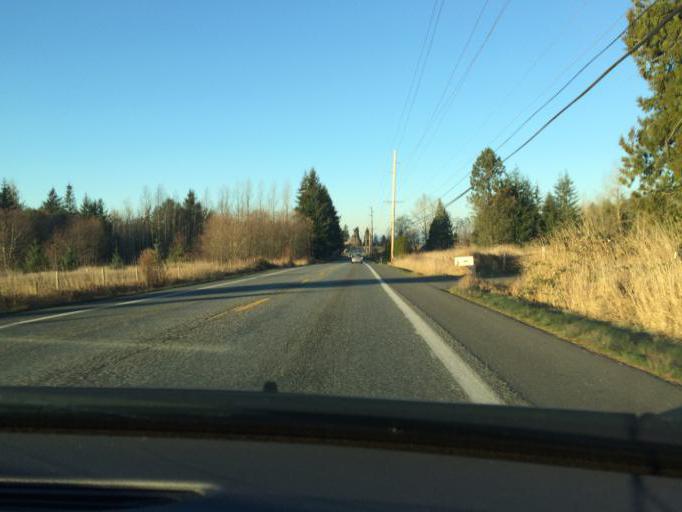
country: US
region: Washington
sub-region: Whatcom County
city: Bellingham
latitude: 48.8434
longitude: -122.4429
